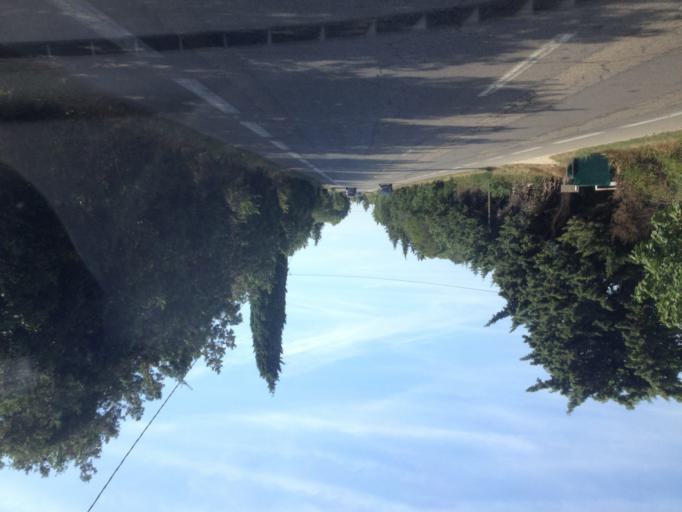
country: FR
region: Provence-Alpes-Cote d'Azur
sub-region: Departement du Vaucluse
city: Carpentras
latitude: 44.0733
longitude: 5.0416
